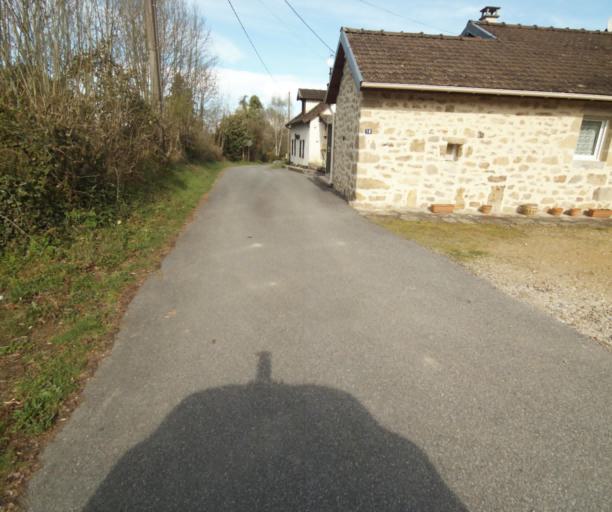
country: FR
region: Limousin
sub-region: Departement de la Correze
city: Correze
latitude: 45.3456
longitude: 1.8521
